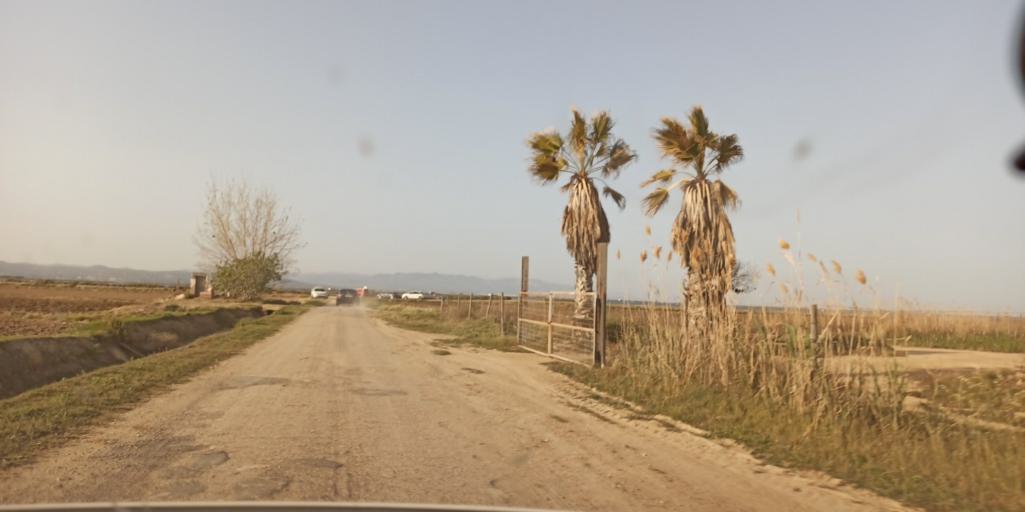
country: ES
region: Catalonia
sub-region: Provincia de Tarragona
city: Deltebre
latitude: 40.7615
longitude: 0.7543
